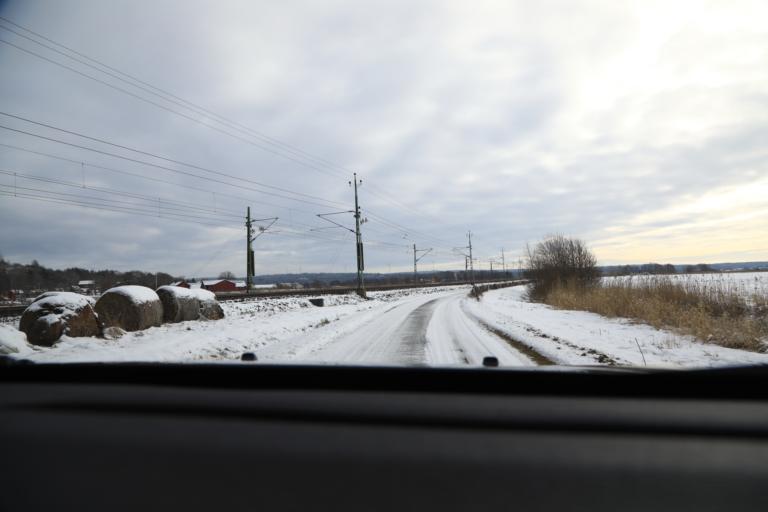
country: SE
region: Halland
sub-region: Kungsbacka Kommun
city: Frillesas
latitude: 57.2327
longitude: 12.2047
